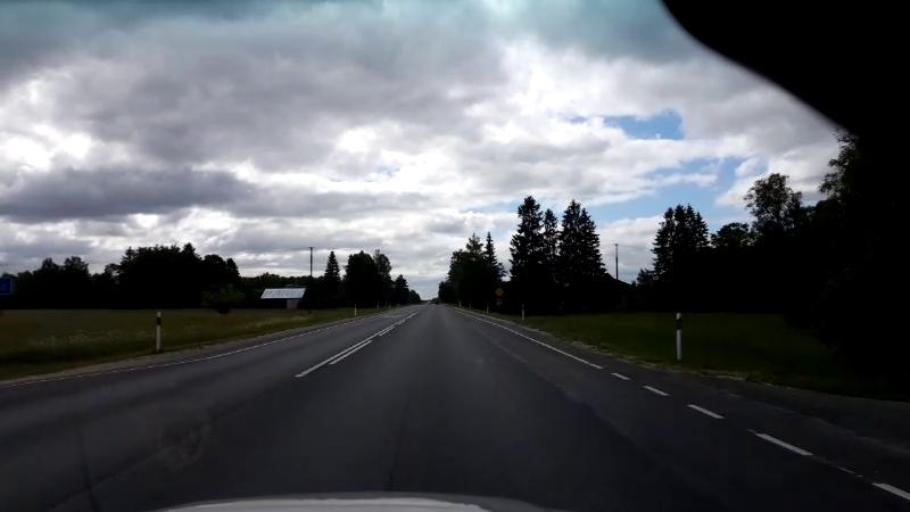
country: EE
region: Paernumaa
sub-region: Halinga vald
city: Parnu-Jaagupi
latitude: 58.6537
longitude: 24.4768
